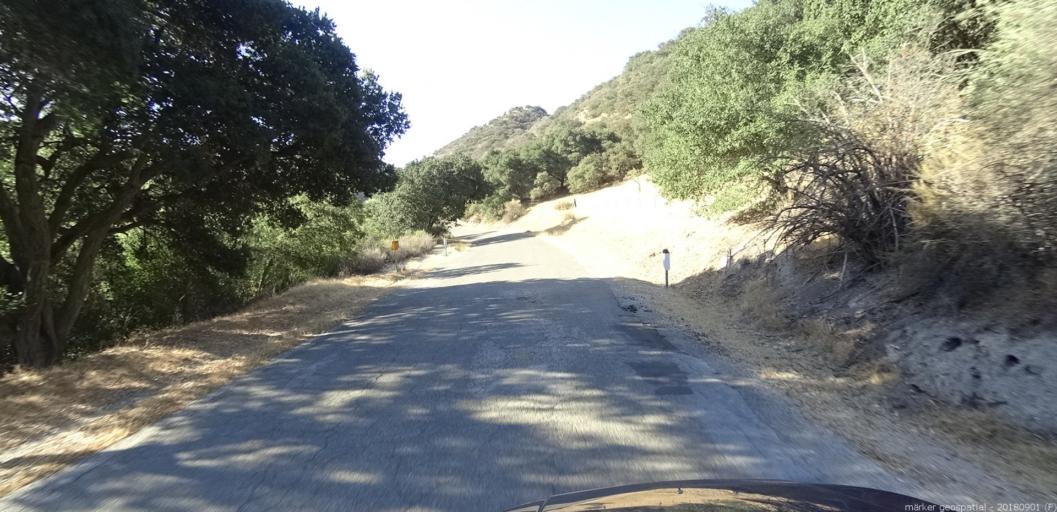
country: US
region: California
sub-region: Monterey County
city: Greenfield
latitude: 36.2229
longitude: -121.2793
